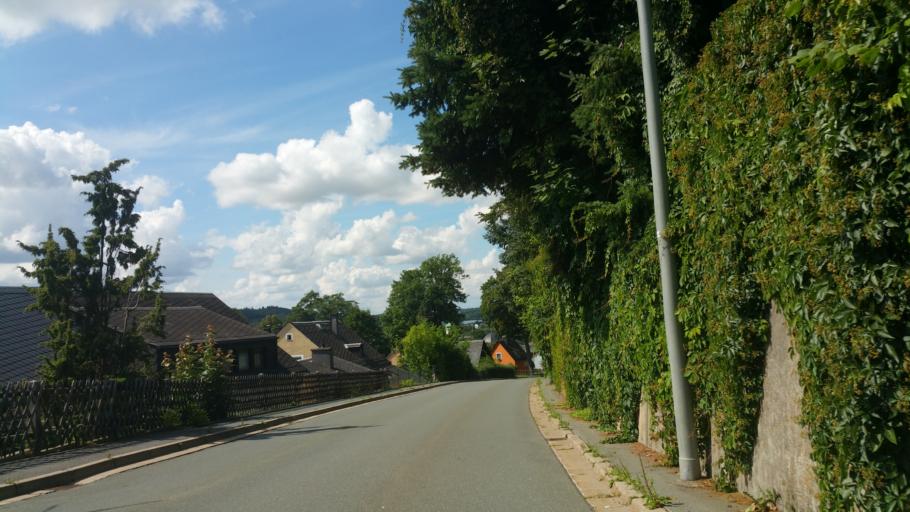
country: DE
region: Bavaria
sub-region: Upper Franconia
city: Oberkotzau
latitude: 50.2597
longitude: 11.9371
